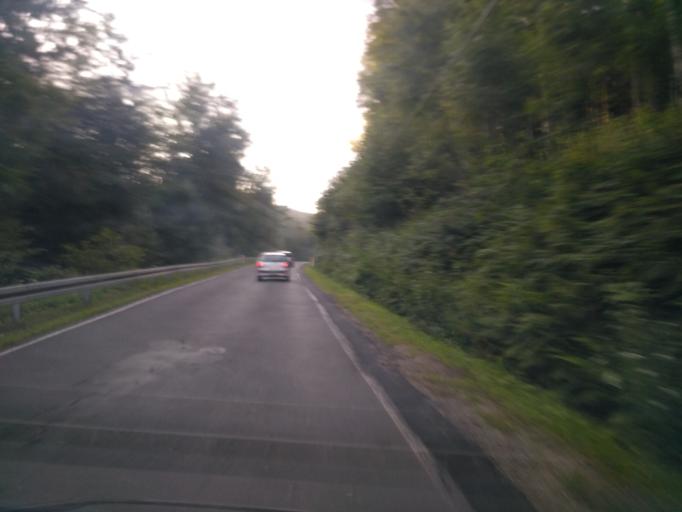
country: PL
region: Subcarpathian Voivodeship
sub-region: Powiat krosnienski
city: Korczyna
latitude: 49.7556
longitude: 21.7953
